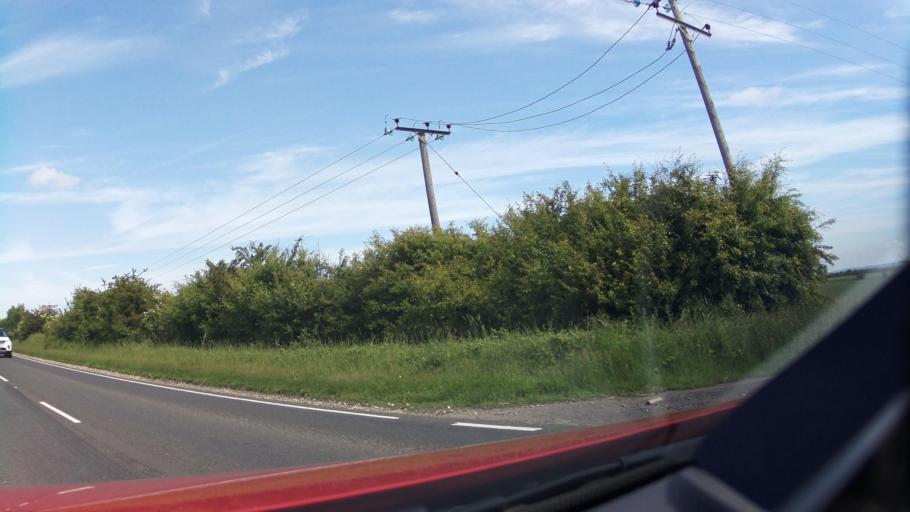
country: GB
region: England
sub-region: Lincolnshire
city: Burton
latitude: 53.3244
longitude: -0.5375
